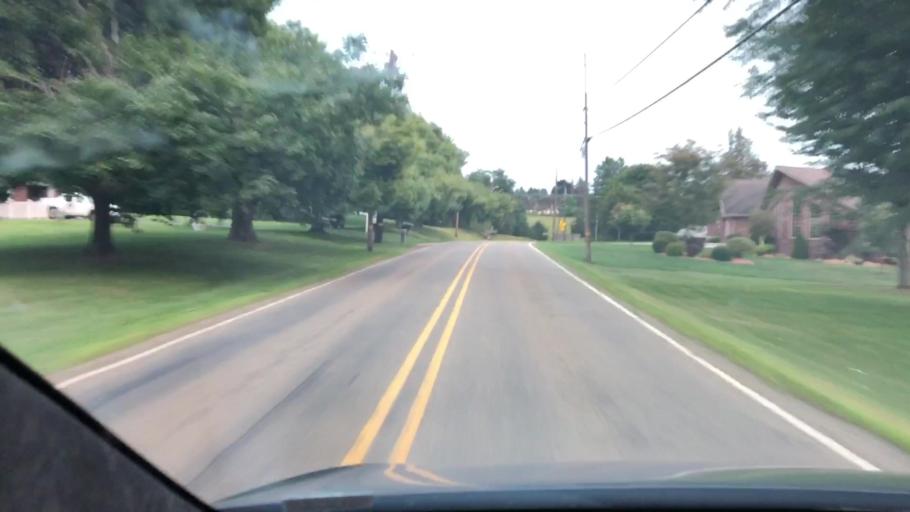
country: US
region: Pennsylvania
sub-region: Butler County
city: Homeacre-Lyndora
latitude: 40.8842
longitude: -79.9191
